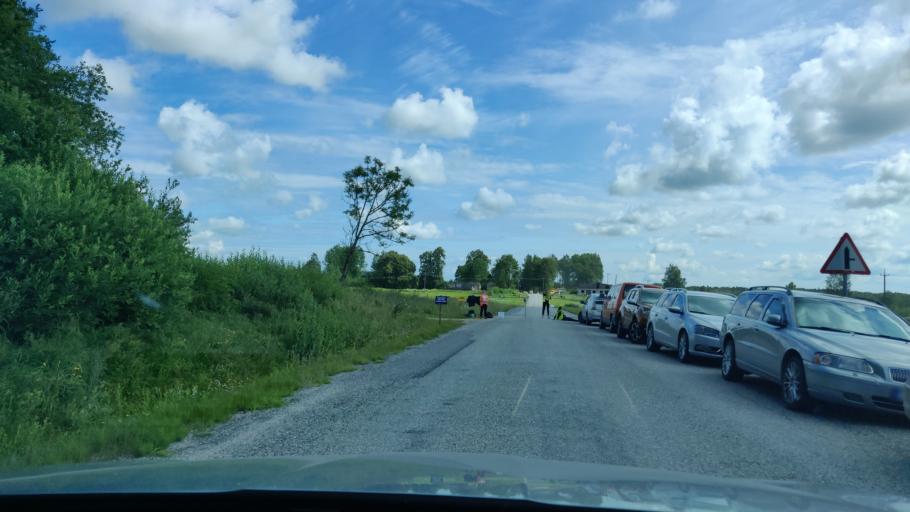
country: EE
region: Tartu
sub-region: Elva linn
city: Elva
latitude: 58.0265
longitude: 26.3435
